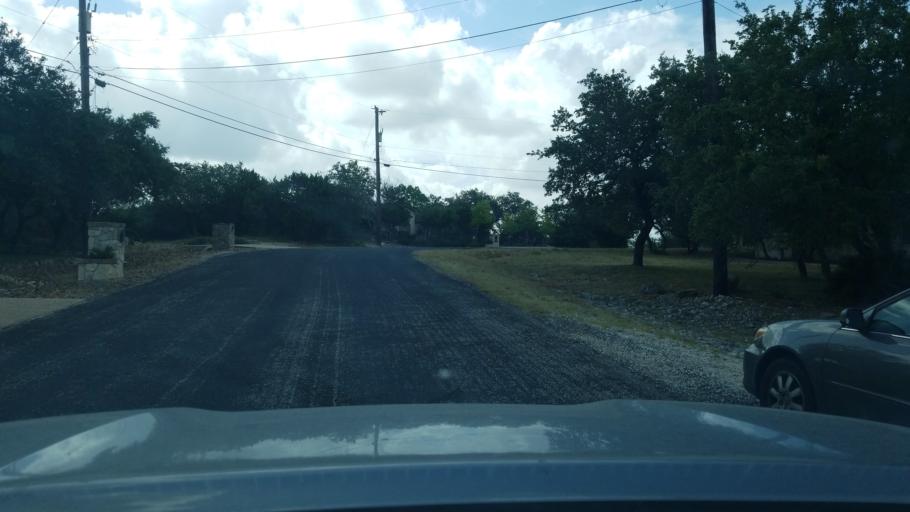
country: US
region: Texas
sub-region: Bexar County
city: Timberwood Park
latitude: 29.6887
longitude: -98.5130
